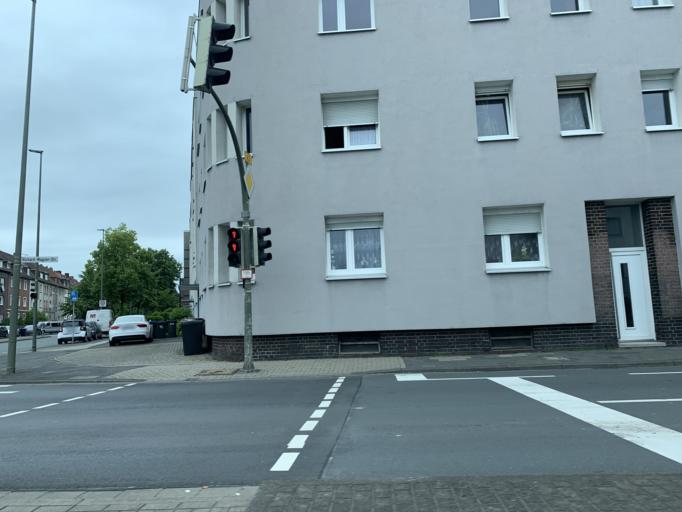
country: DE
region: North Rhine-Westphalia
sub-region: Regierungsbezirk Arnsberg
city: Hamm
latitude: 51.6696
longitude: 7.8198
